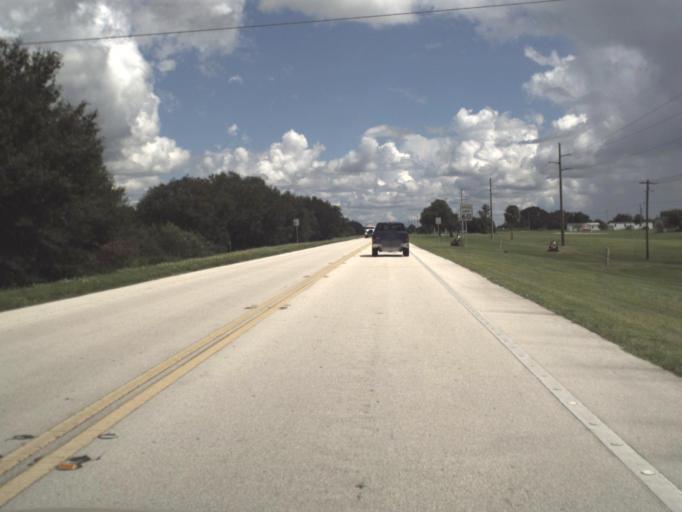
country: US
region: Florida
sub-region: DeSoto County
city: Southeast Arcadia
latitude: 27.2095
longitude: -81.6619
